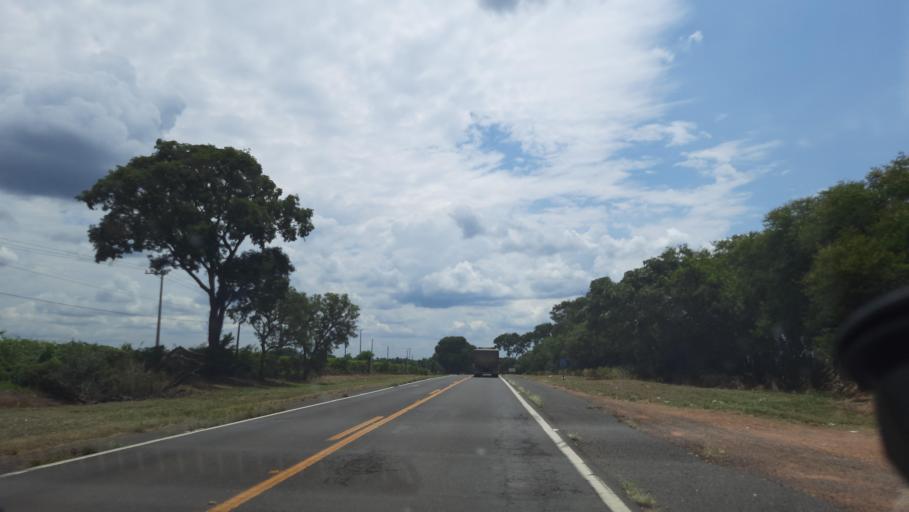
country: BR
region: Sao Paulo
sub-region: Mococa
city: Mococa
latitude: -21.5127
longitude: -47.0394
